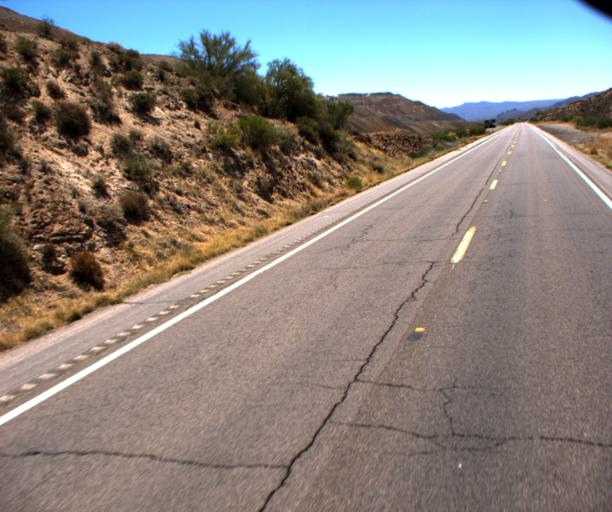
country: US
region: Arizona
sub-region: Pinal County
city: Kearny
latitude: 33.1530
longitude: -110.9953
